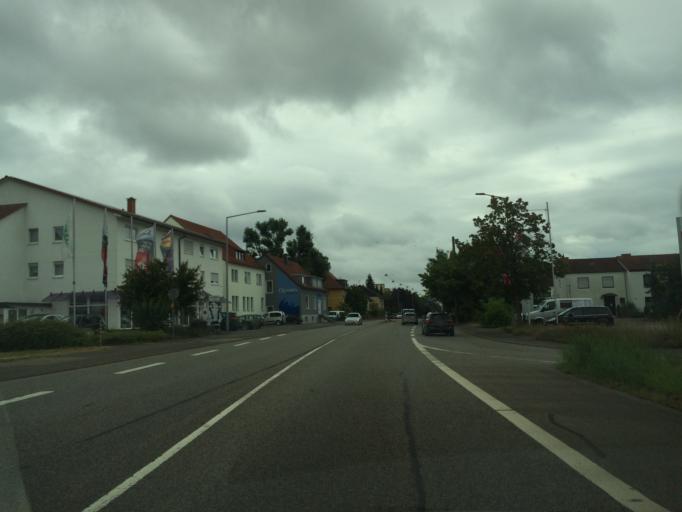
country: DE
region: Saarland
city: Dillingen
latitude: 49.3660
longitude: 6.7127
